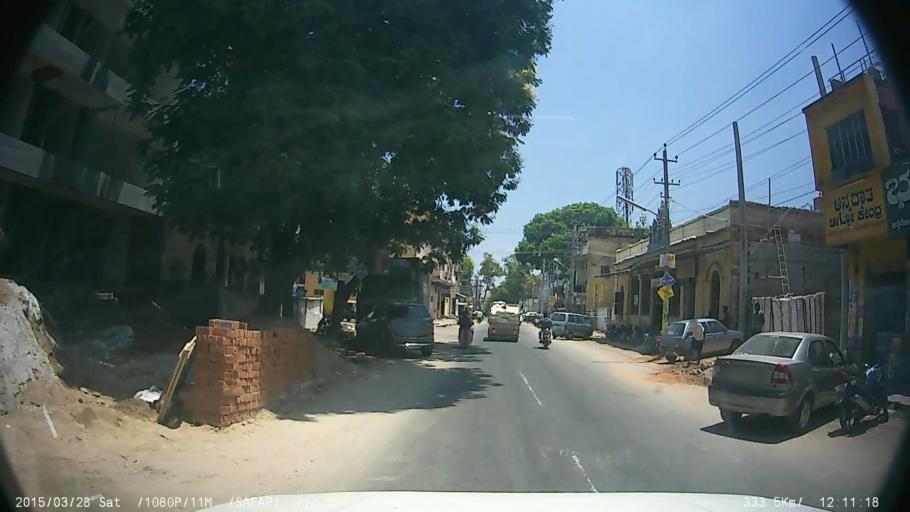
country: IN
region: Karnataka
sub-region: Mysore
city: Mysore
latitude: 12.3055
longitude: 76.6500
